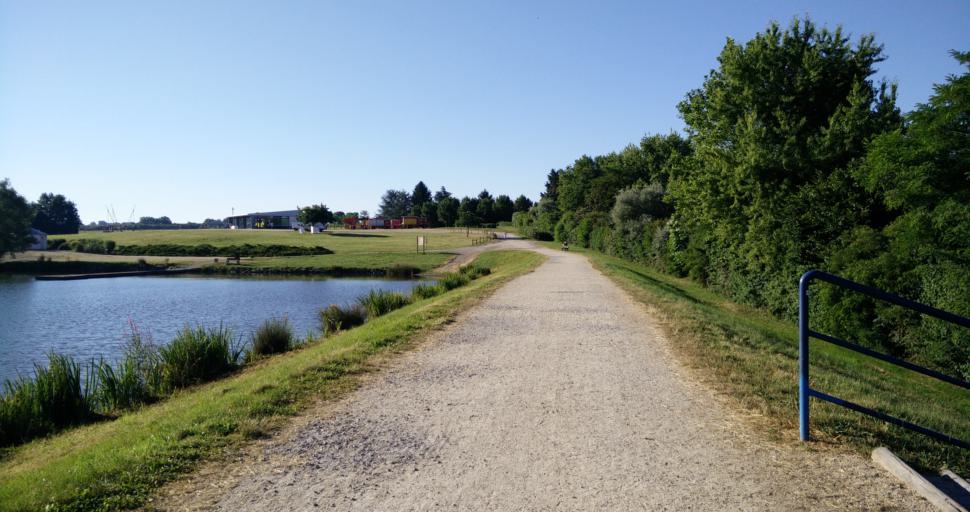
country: FR
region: Auvergne
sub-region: Departement de l'Allier
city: Yzeure
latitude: 46.5449
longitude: 3.3699
